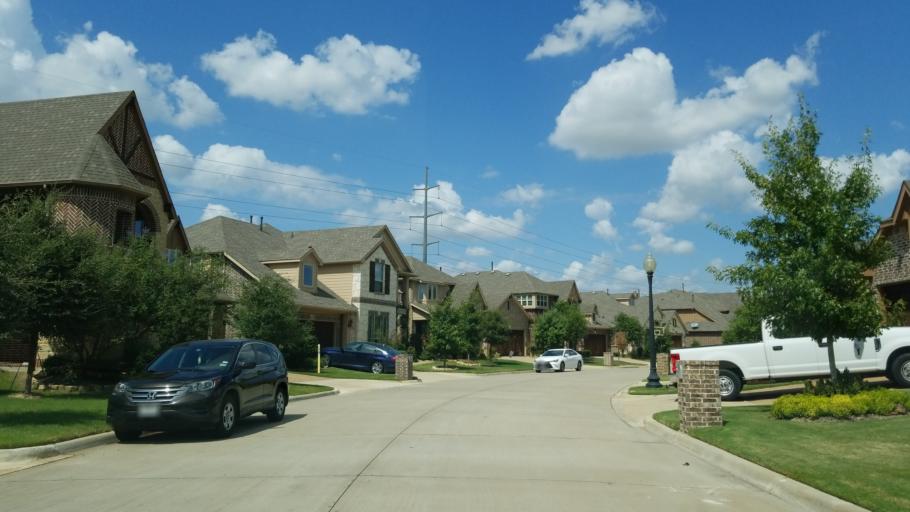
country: US
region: Texas
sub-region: Tarrant County
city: Euless
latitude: 32.8745
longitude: -97.0949
